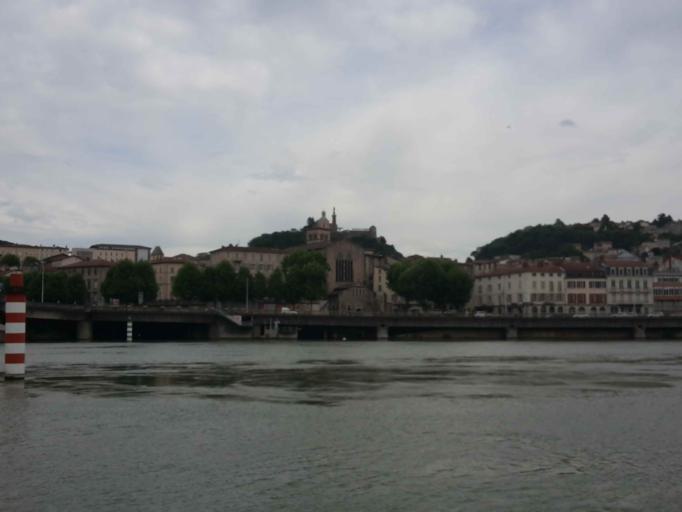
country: FR
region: Rhone-Alpes
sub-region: Departement du Rhone
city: Sainte-Colombe
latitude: 45.5284
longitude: 4.8712
